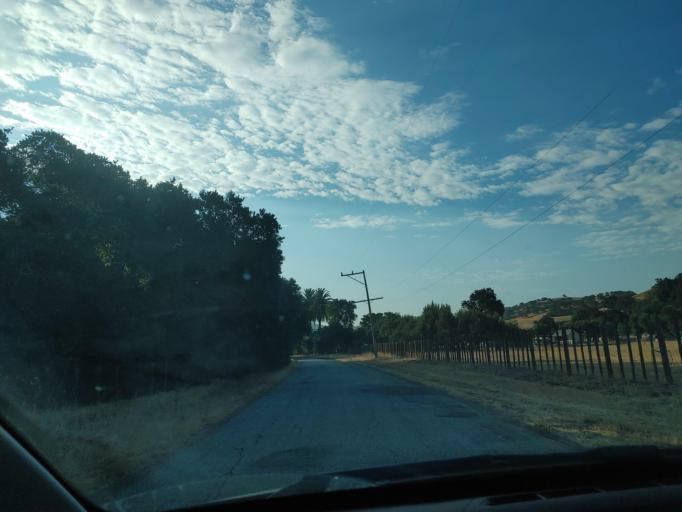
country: US
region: California
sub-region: San Benito County
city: Ridgemark
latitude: 36.7856
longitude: -121.2549
